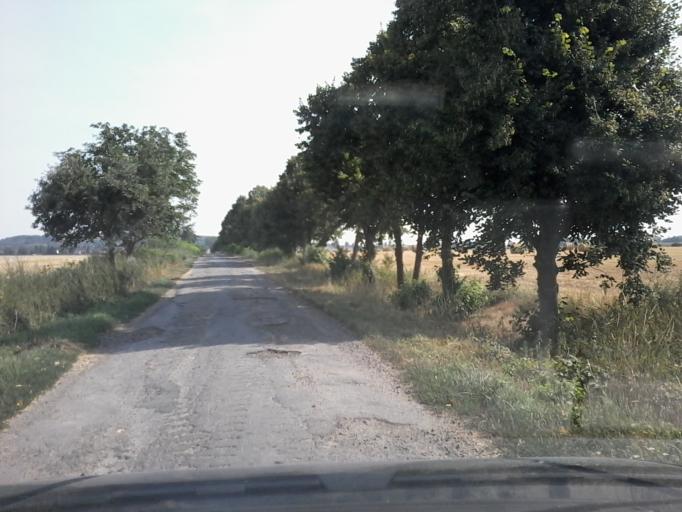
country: HU
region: Vas
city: Janoshaza
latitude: 47.1723
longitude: 17.0906
